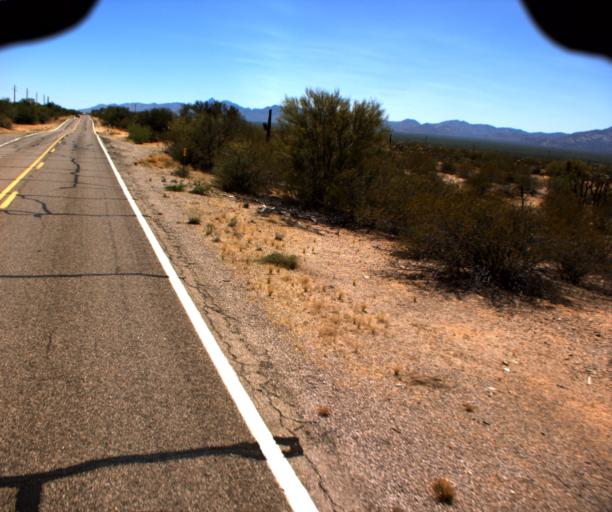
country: US
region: Arizona
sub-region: Pima County
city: Three Points
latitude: 32.0062
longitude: -111.3582
